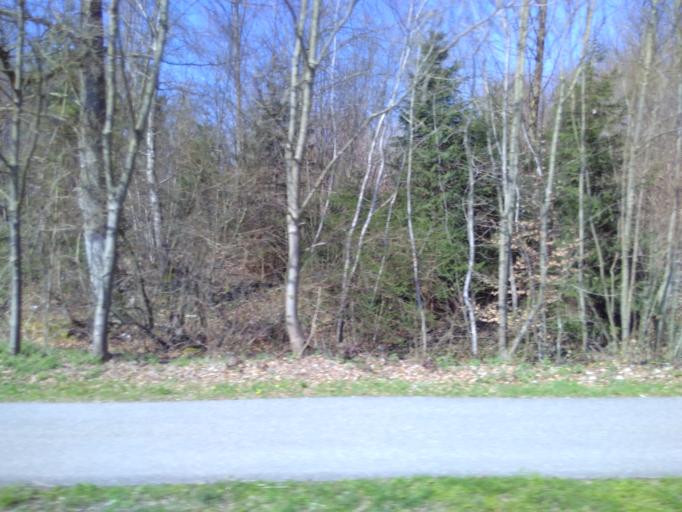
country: CH
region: Saint Gallen
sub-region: Wahlkreis See-Gaster
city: Eschenbach
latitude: 47.2318
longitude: 8.9015
